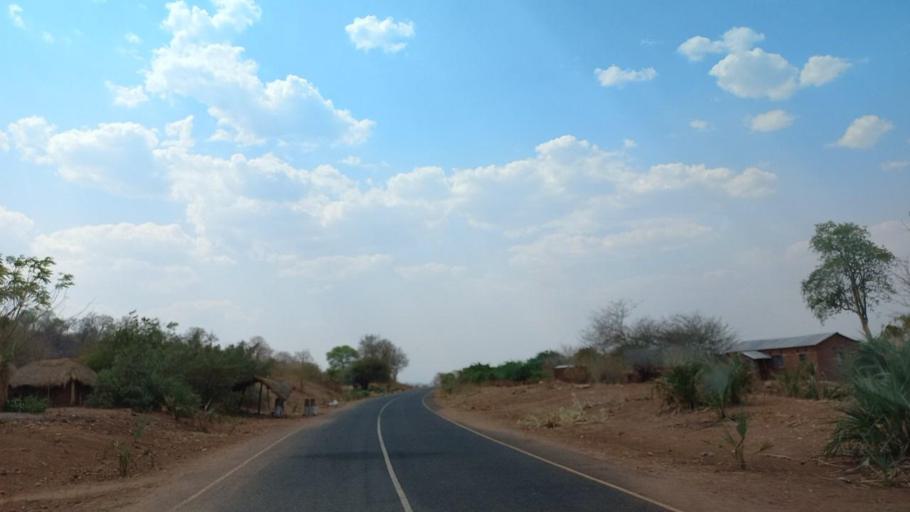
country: ZM
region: Lusaka
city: Luangwa
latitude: -15.3164
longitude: 30.3309
